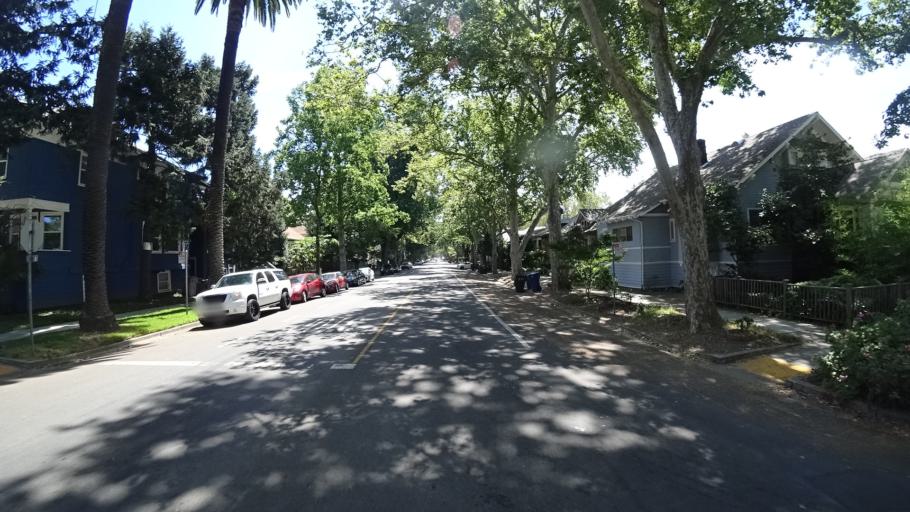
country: US
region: California
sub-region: Sacramento County
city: Sacramento
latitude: 38.5818
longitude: -121.4762
